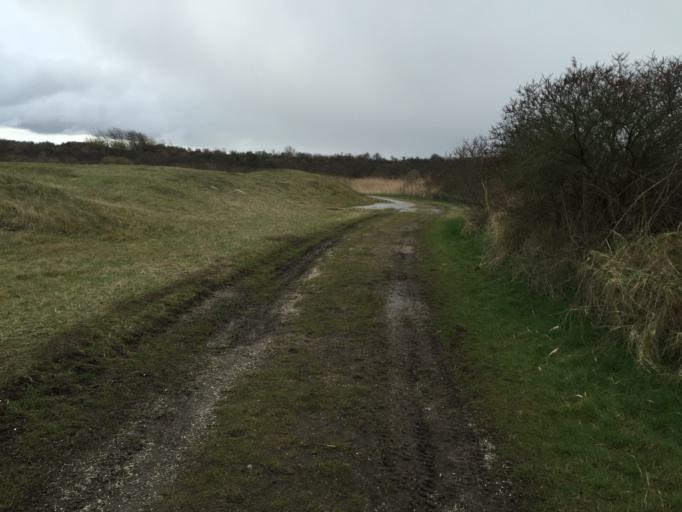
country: NL
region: South Holland
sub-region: Gemeente Goeree-Overflakkee
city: Goedereede
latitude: 51.8390
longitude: 3.9768
